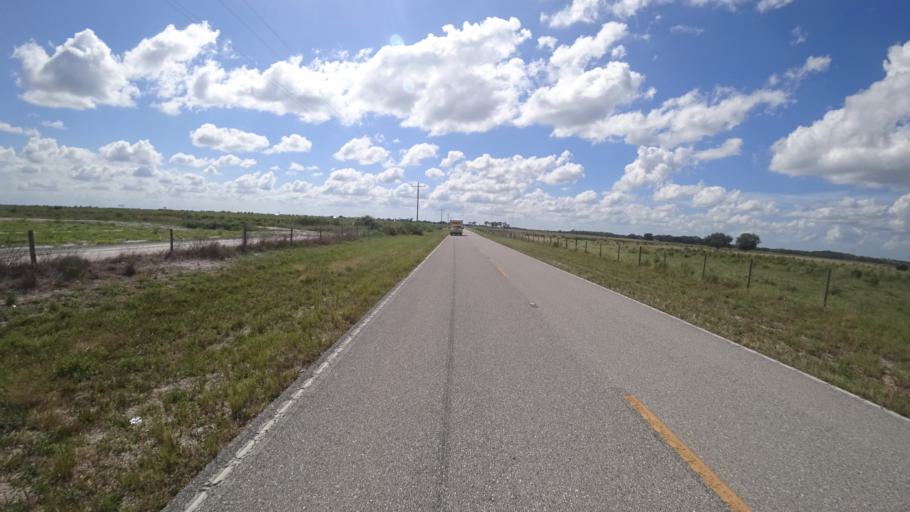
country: US
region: Florida
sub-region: Sarasota County
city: Lake Sarasota
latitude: 27.3121
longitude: -82.1796
